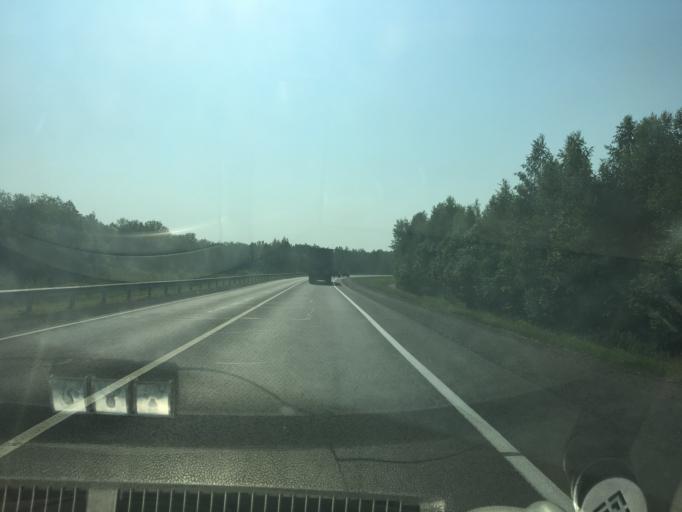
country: RU
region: Nizjnij Novgorod
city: Pamyat' Parizhskoy Kommuny
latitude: 56.0808
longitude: 44.3602
